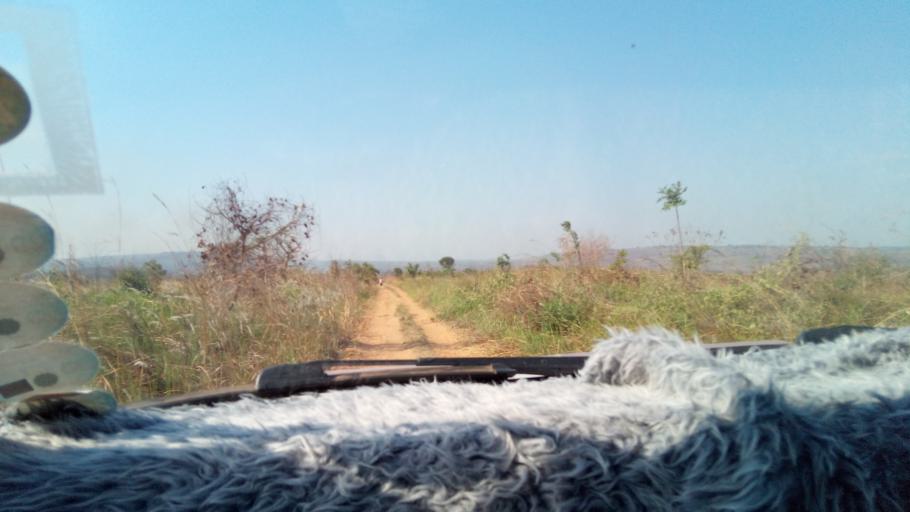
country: CD
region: Katanga
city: Kalemie
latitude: -5.9170
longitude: 29.1234
